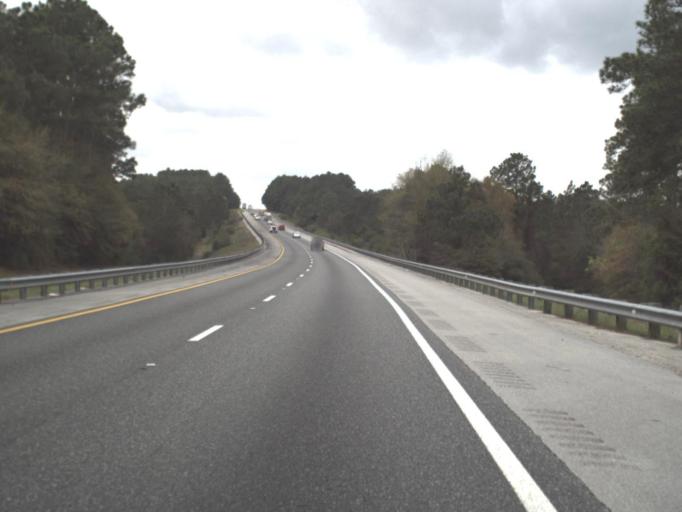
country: US
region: Florida
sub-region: Okaloosa County
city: Crestview
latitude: 30.7243
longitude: -86.5914
